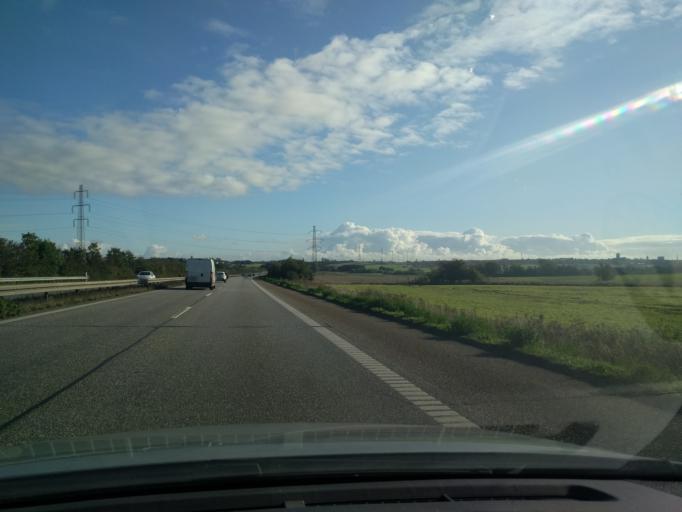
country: DK
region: Zealand
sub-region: Ringsted Kommune
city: Ringsted
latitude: 55.4548
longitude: 11.7426
